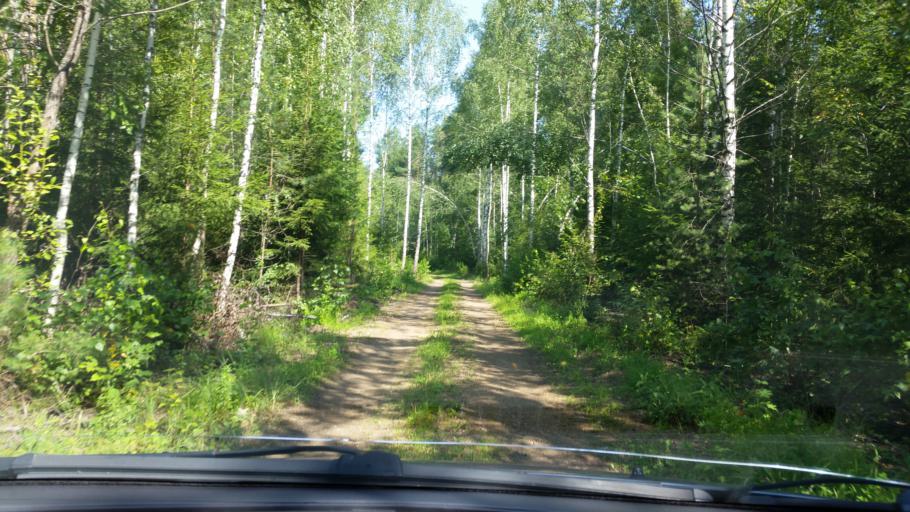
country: RU
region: Moskovskaya
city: Bol'shoye Gryzlovo
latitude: 54.9015
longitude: 37.7639
